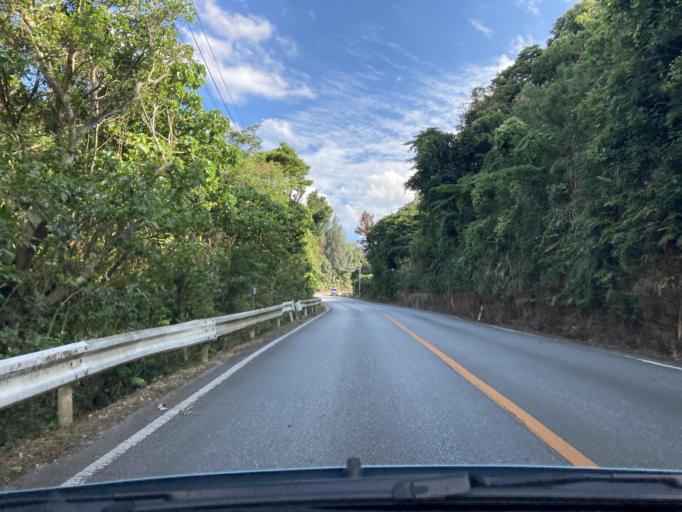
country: JP
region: Okinawa
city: Ishikawa
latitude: 26.4367
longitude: 127.8056
